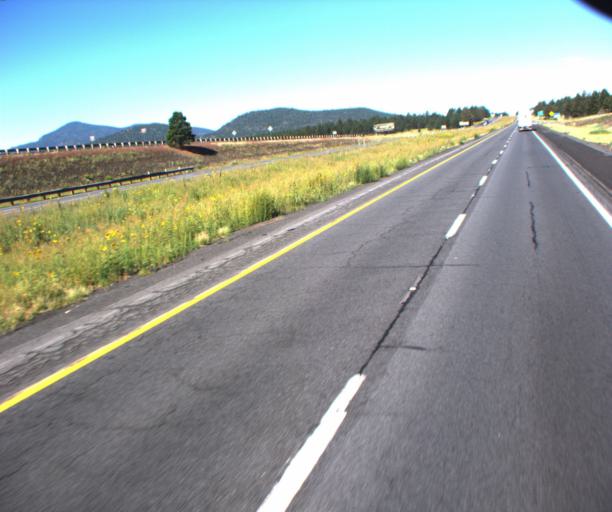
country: US
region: Arizona
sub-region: Coconino County
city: Williams
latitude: 35.2584
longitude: -112.1224
